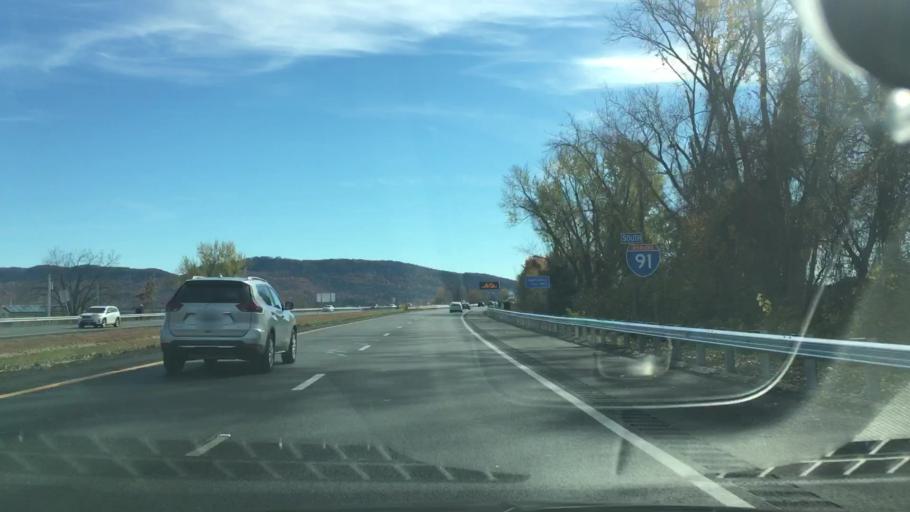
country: US
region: Massachusetts
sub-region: Hampshire County
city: Northampton
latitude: 42.3298
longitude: -72.6183
